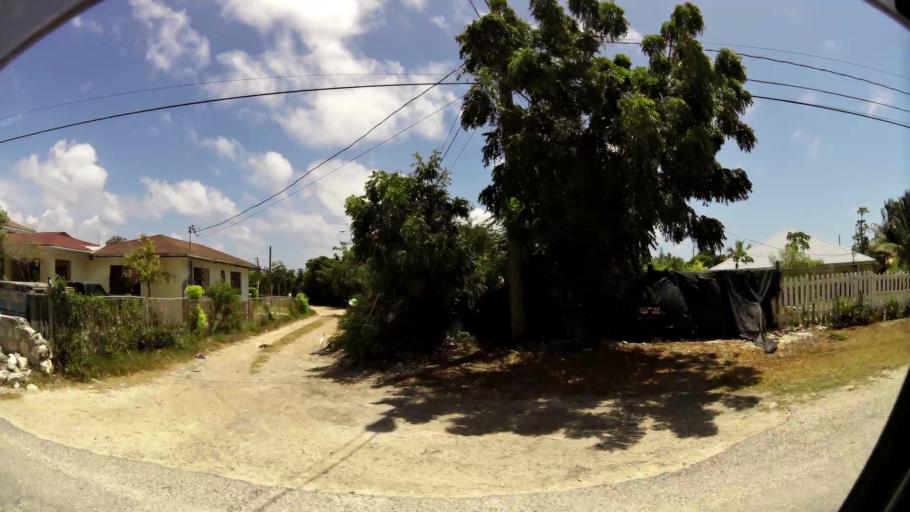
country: TC
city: Cockburn Town
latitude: 21.4511
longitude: -71.1468
